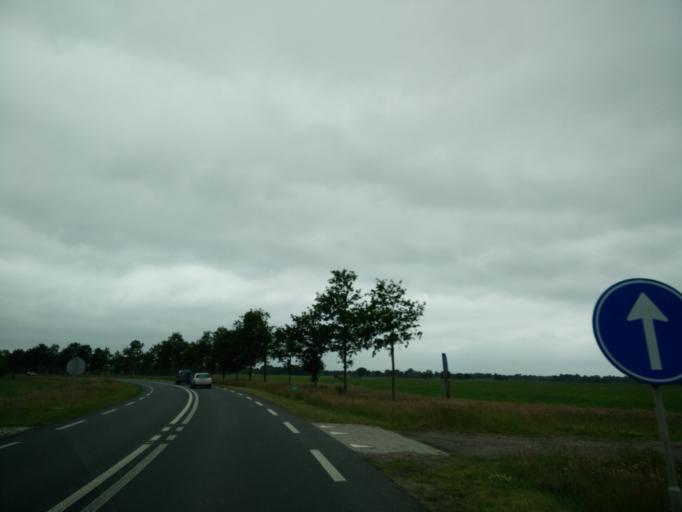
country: NL
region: Groningen
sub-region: Gemeente Groningen
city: Groningen
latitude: 53.1545
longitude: 6.4857
